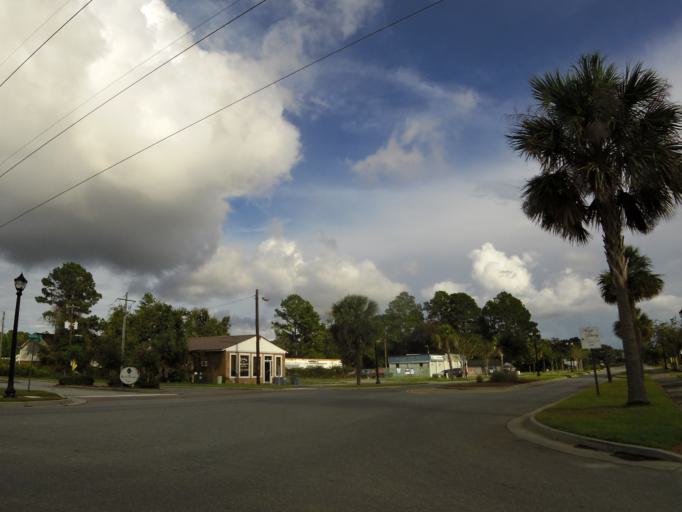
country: US
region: Georgia
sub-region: Liberty County
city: Hinesville
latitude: 31.8547
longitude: -81.6035
